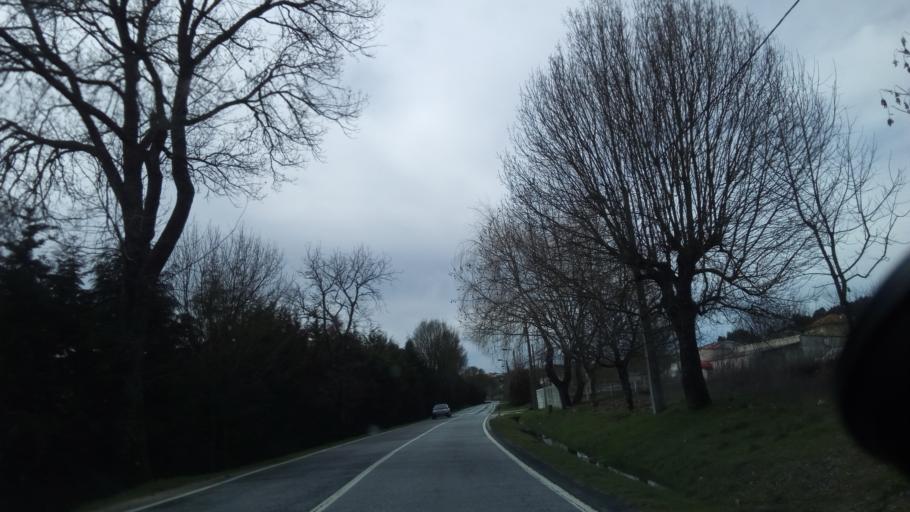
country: PT
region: Guarda
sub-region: Seia
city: Seia
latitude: 40.4539
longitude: -7.7010
